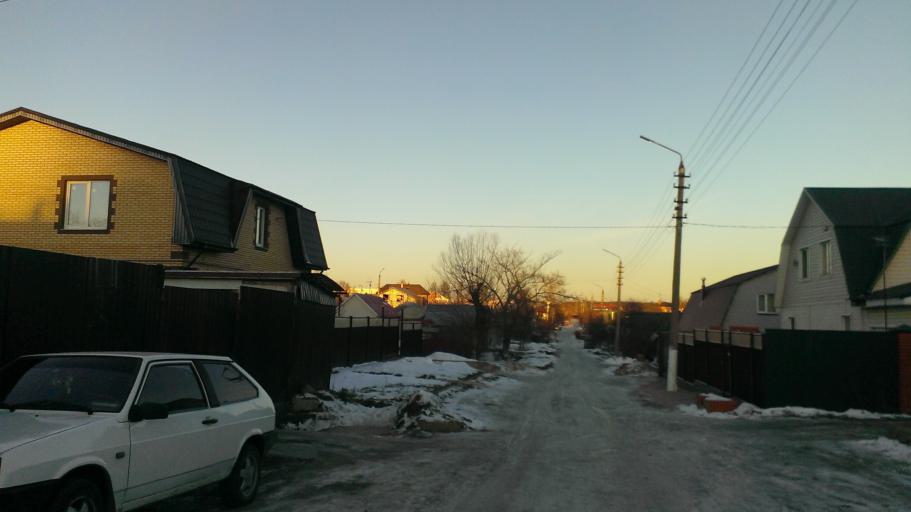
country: RU
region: Tula
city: Tula
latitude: 54.1973
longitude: 37.6941
